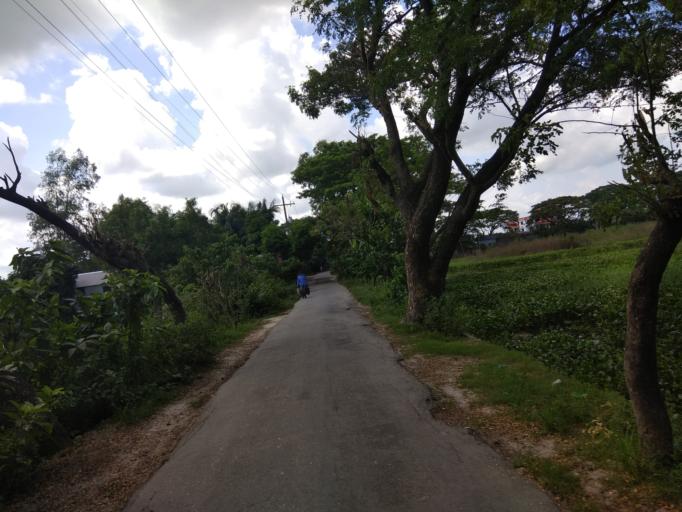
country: BD
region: Dhaka
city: Narayanganj
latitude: 23.4573
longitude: 90.4525
